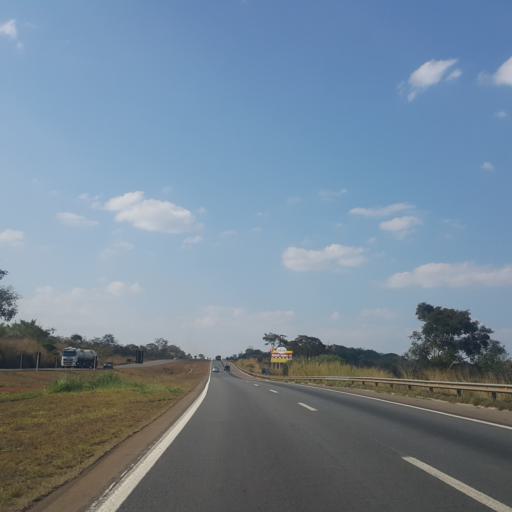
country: BR
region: Goias
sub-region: Abadiania
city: Abadiania
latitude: -16.2714
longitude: -48.7706
